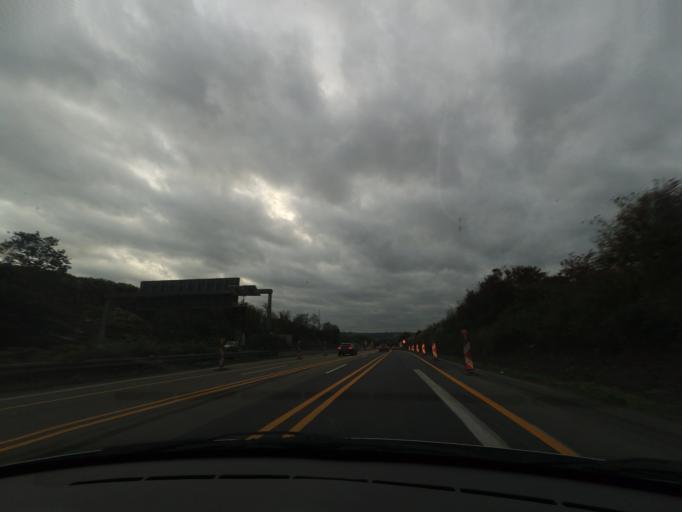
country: DE
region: North Rhine-Westphalia
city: Herdecke
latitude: 51.4026
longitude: 7.4654
